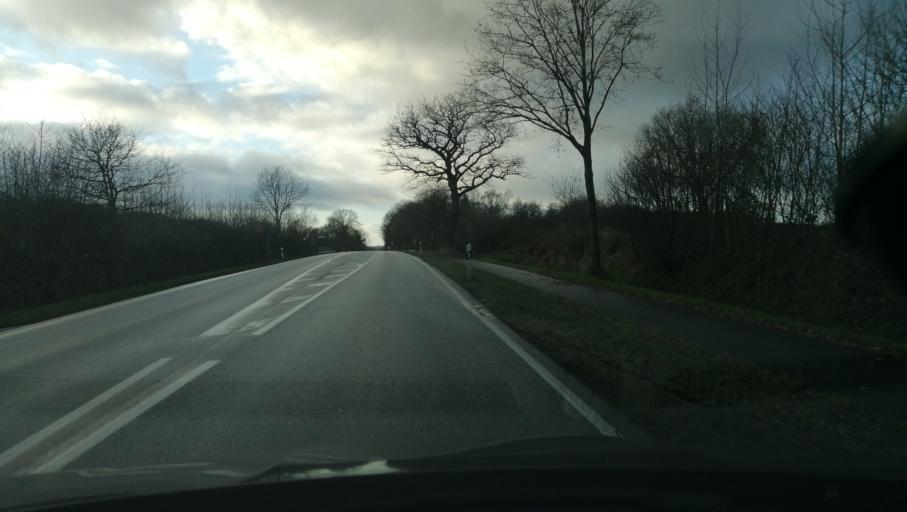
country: DE
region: Schleswig-Holstein
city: Tensbuttel-Rost
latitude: 54.1128
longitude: 9.2250
